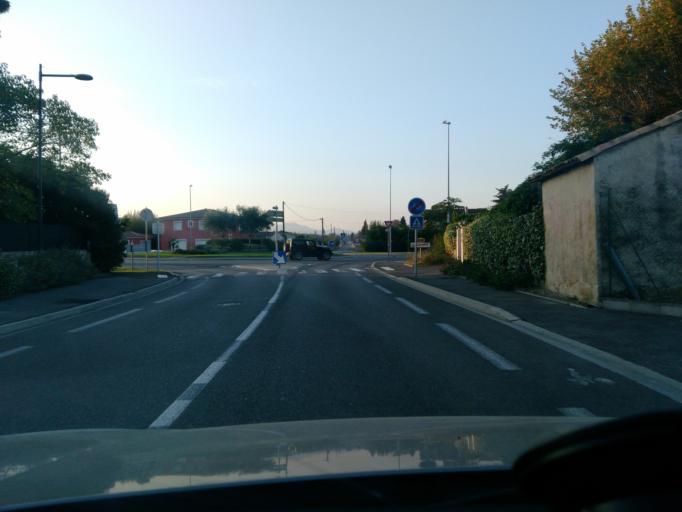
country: FR
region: Rhone-Alpes
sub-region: Departement de la Drome
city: Montelimar
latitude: 44.5319
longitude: 4.7518
